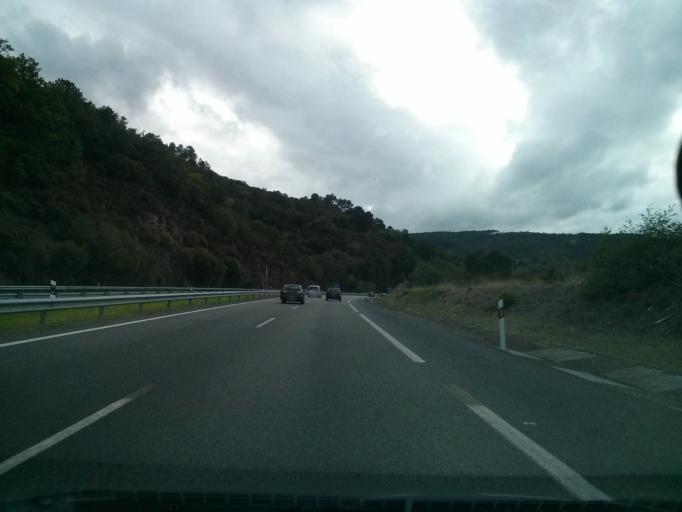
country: ES
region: Galicia
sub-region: Provincia de Ourense
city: Toen
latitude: 42.3322
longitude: -7.9482
